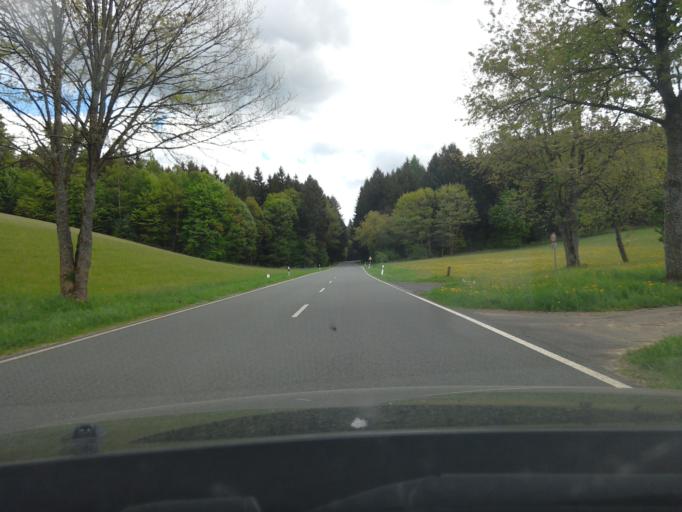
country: DE
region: Bavaria
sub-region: Regierungsbezirk Unterfranken
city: Frammersbach
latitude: 50.1571
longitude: 9.4789
